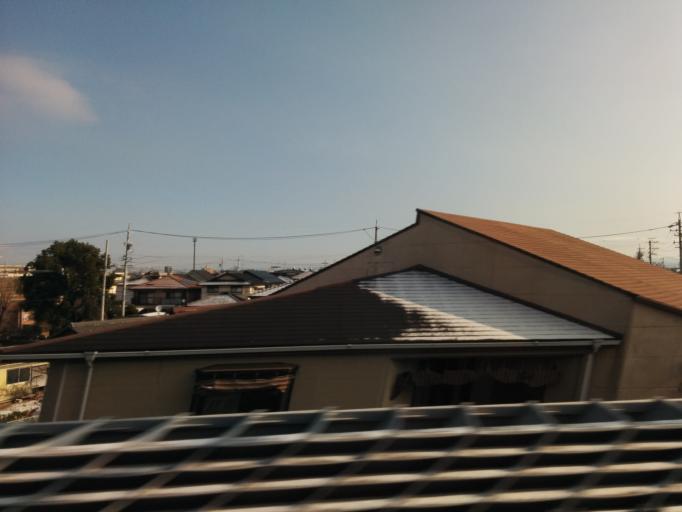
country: JP
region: Aichi
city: Chiryu
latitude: 34.9833
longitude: 137.0469
